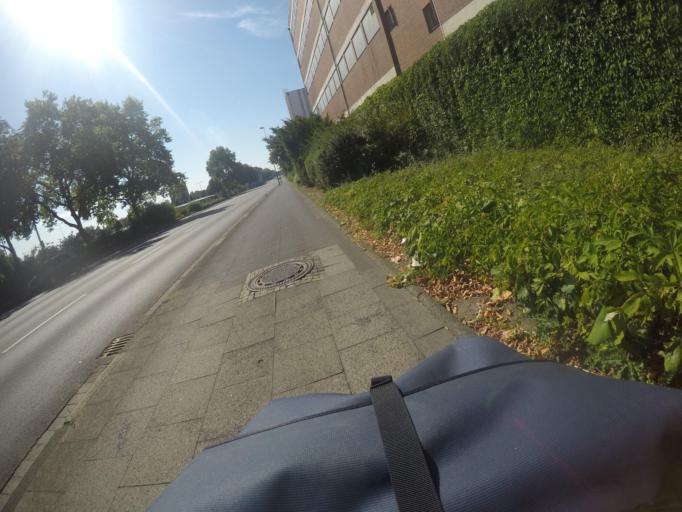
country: DE
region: North Rhine-Westphalia
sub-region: Regierungsbezirk Koln
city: Leverkusen
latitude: 51.0212
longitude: 6.9900
